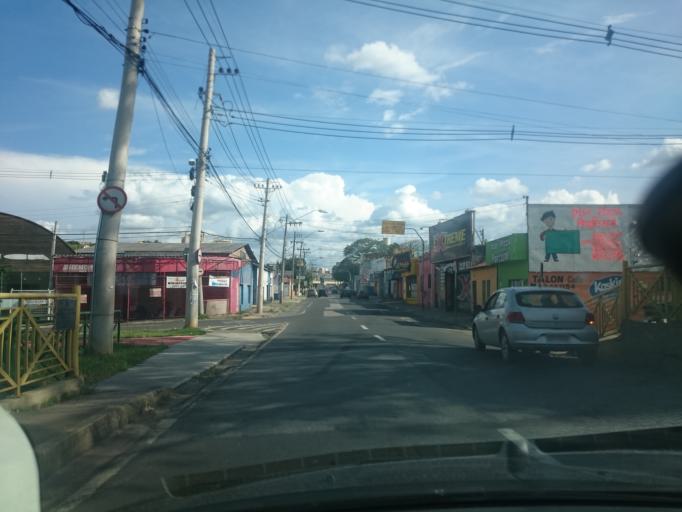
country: BR
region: Sao Paulo
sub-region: Sorocaba
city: Sorocaba
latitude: -23.4919
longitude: -47.4428
